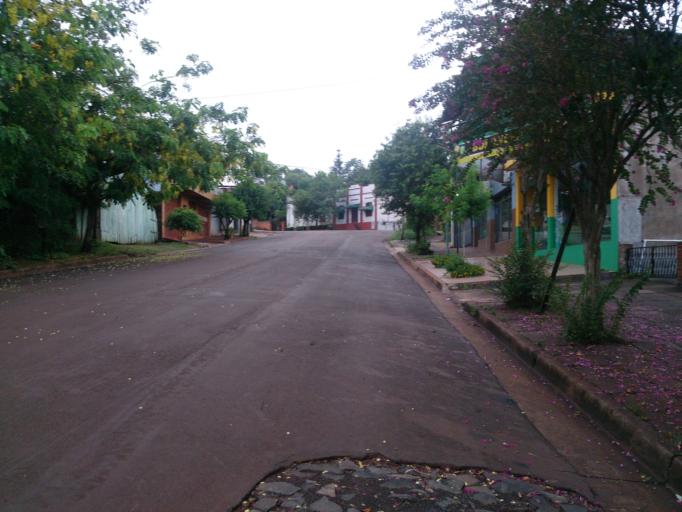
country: AR
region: Misiones
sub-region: Departamento de Obera
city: Obera
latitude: -27.4905
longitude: -55.1187
